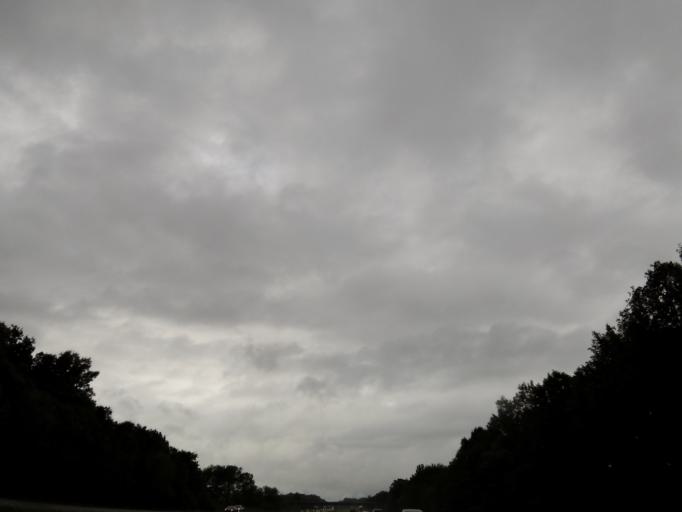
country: US
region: Illinois
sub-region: Jefferson County
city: Mount Vernon
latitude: 38.3516
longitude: -88.9882
